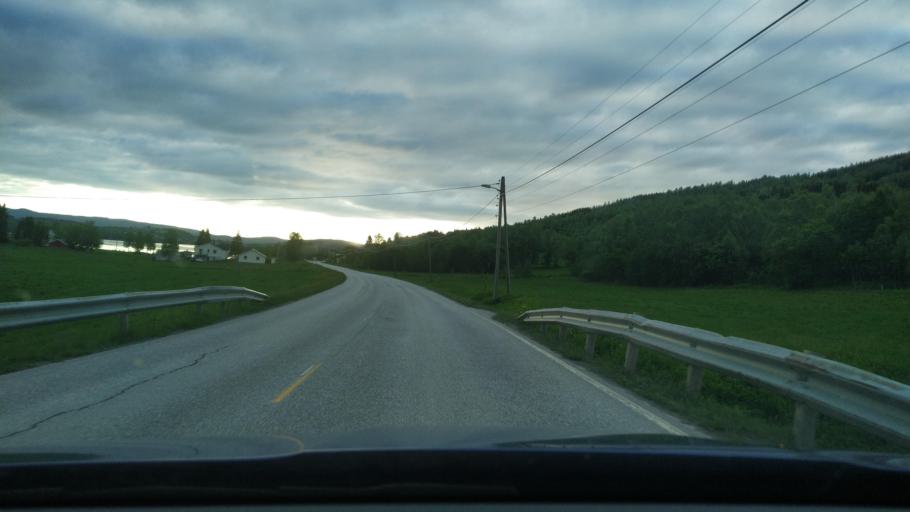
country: NO
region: Troms
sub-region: Sorreisa
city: Sorreisa
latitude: 69.1268
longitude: 18.2124
